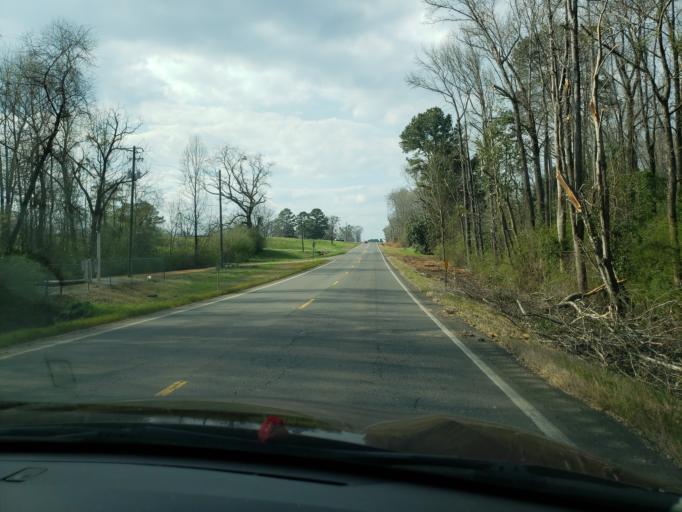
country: US
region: Alabama
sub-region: Hale County
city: Greensboro
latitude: 32.7109
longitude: -87.6119
